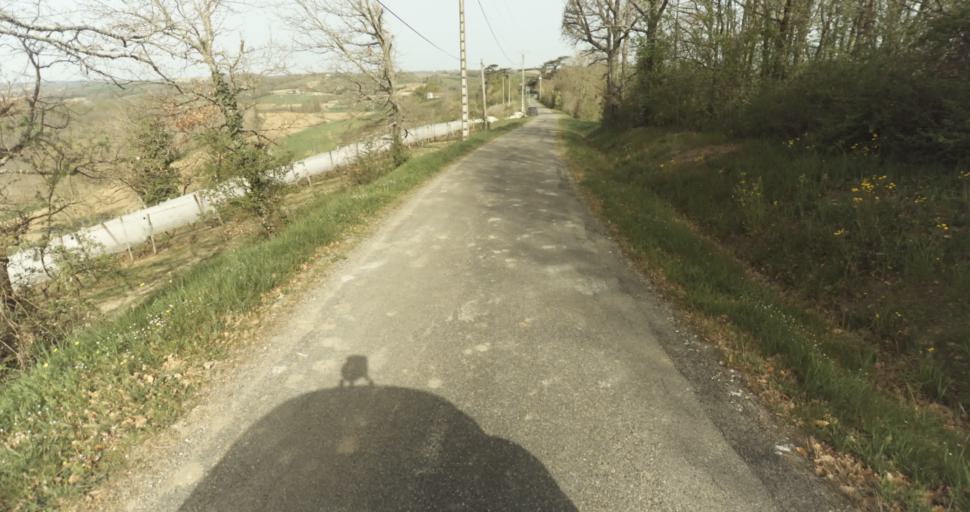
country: FR
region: Midi-Pyrenees
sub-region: Departement du Tarn-et-Garonne
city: Moissac
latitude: 44.1639
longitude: 1.0433
